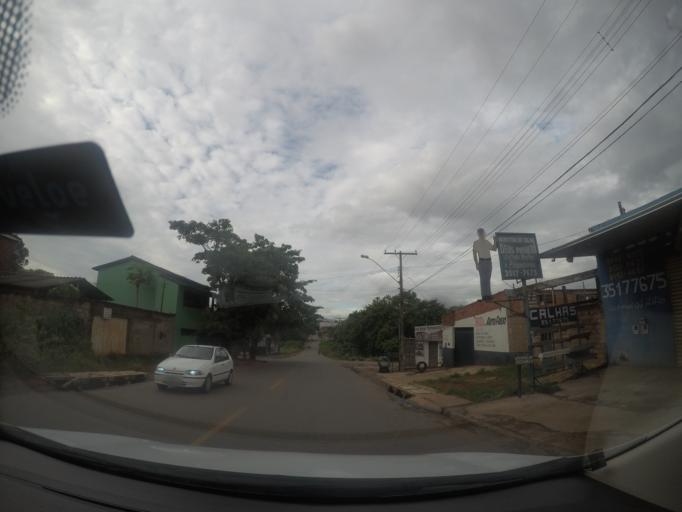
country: BR
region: Goias
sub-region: Goiania
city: Goiania
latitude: -16.6237
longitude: -49.3277
